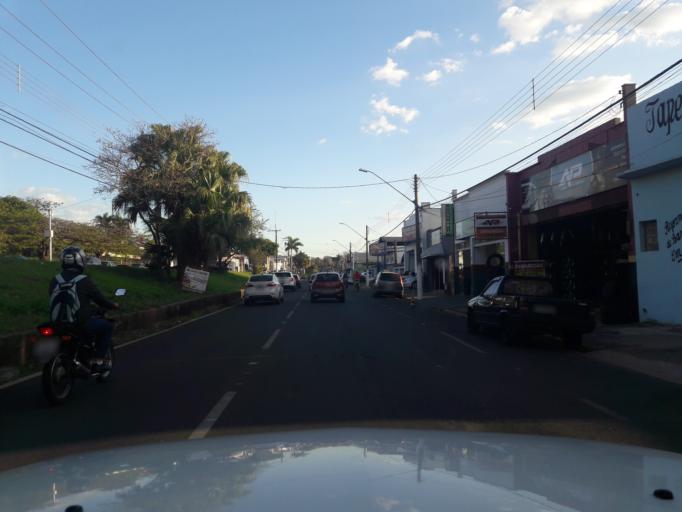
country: BR
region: Sao Paulo
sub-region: Moji-Guacu
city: Mogi-Gaucu
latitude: -22.3927
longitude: -46.9459
